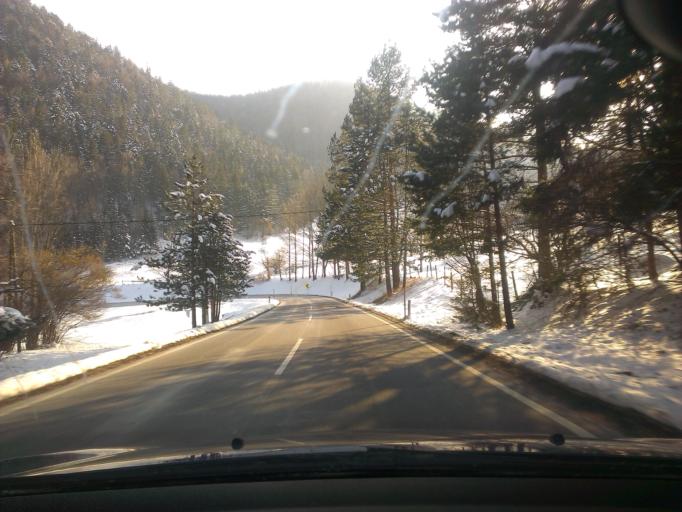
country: AT
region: Lower Austria
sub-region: Politischer Bezirk Wiener Neustadt
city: Miesenbach
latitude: 47.8193
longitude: 15.9521
